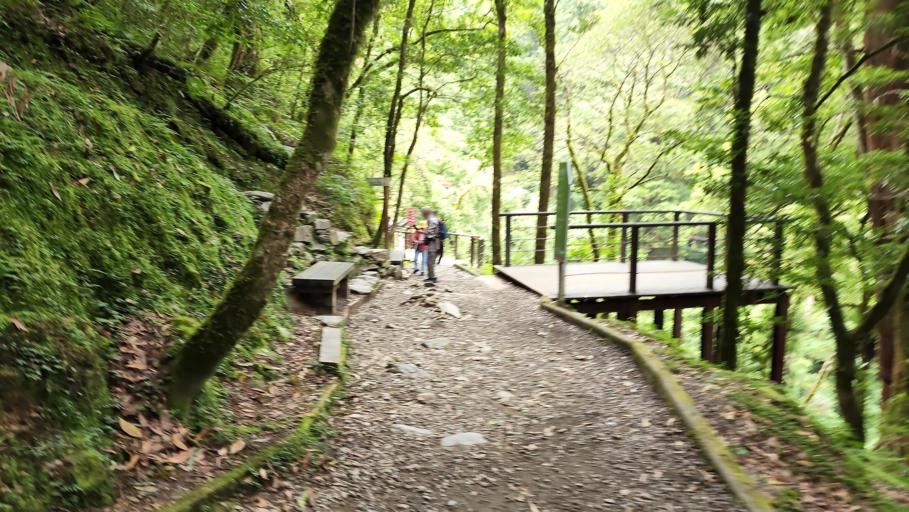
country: TW
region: Taiwan
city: Daxi
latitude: 24.7108
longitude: 121.4403
